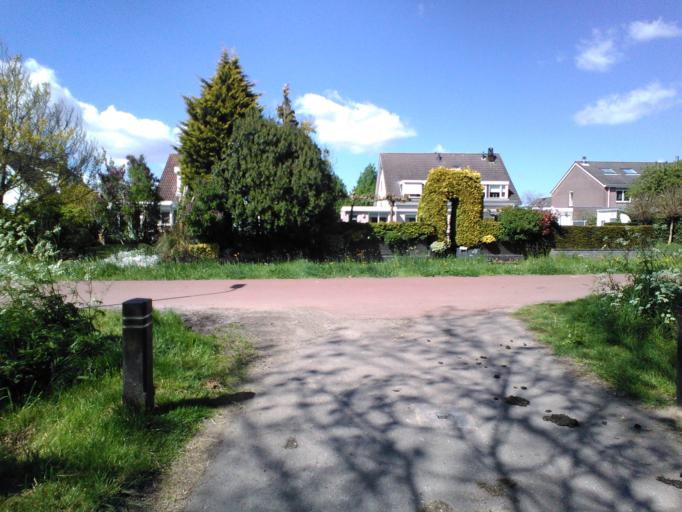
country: NL
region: South Holland
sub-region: Gemeente Hendrik-Ido-Ambacht
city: Hendrik-Ido-Ambacht
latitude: 51.8601
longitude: 4.6243
